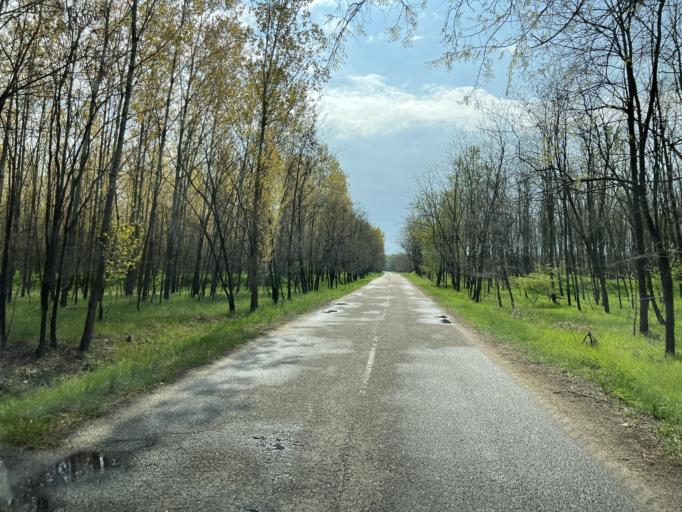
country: HU
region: Pest
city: Hernad
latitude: 47.1759
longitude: 19.4776
